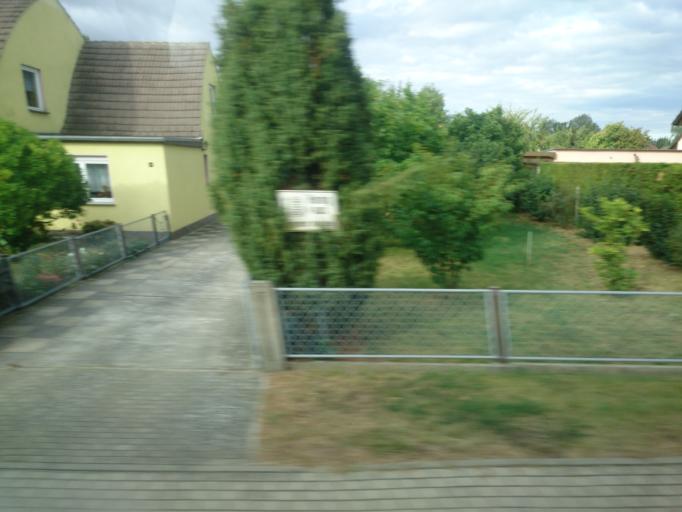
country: DE
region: Mecklenburg-Vorpommern
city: Pasewalk
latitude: 53.5206
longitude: 13.9769
